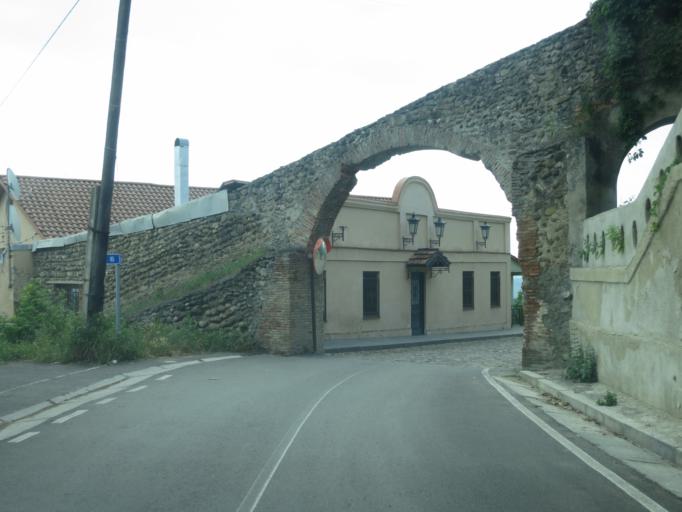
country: GE
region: Kakheti
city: Sighnaghi
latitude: 41.6216
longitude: 45.9222
